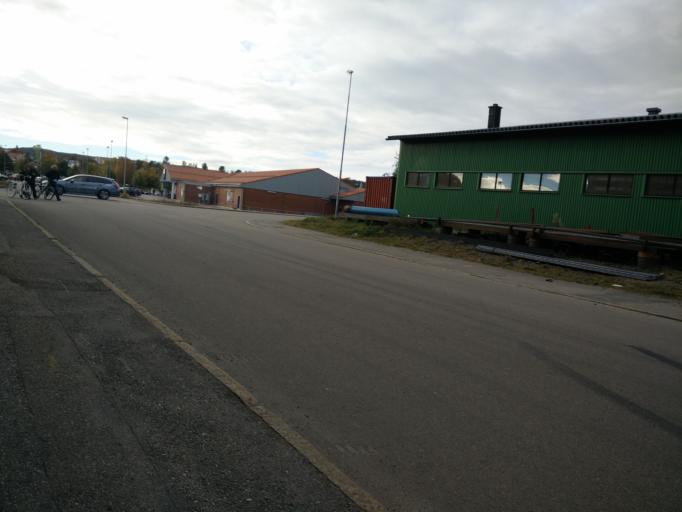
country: SE
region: Vaesternorrland
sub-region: Haernoesands Kommun
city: Haernoesand
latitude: 62.6356
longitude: 17.9363
